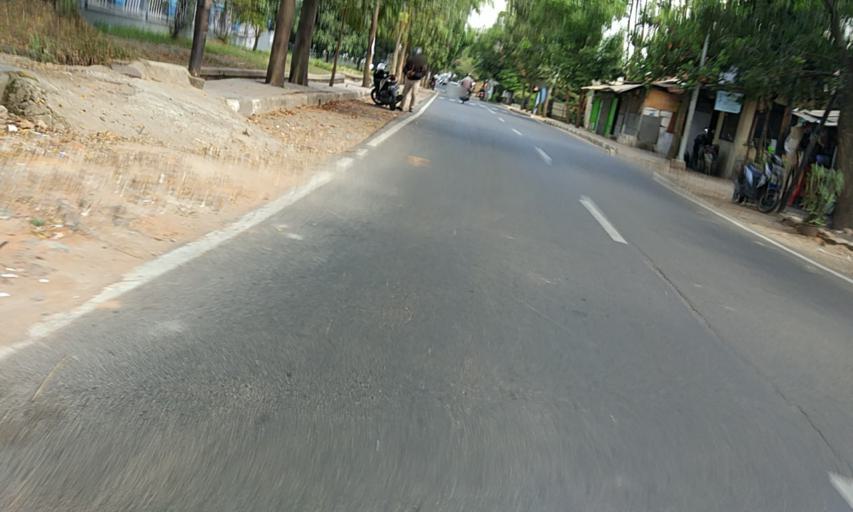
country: ID
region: West Java
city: Bandung
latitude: -6.9060
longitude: 107.6732
